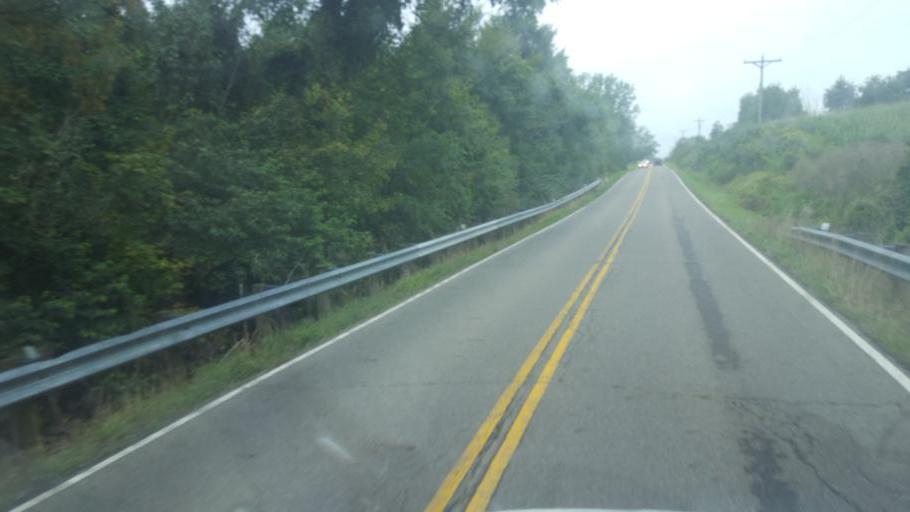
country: US
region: Ohio
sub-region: Licking County
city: Johnstown
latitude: 40.1579
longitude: -82.6382
